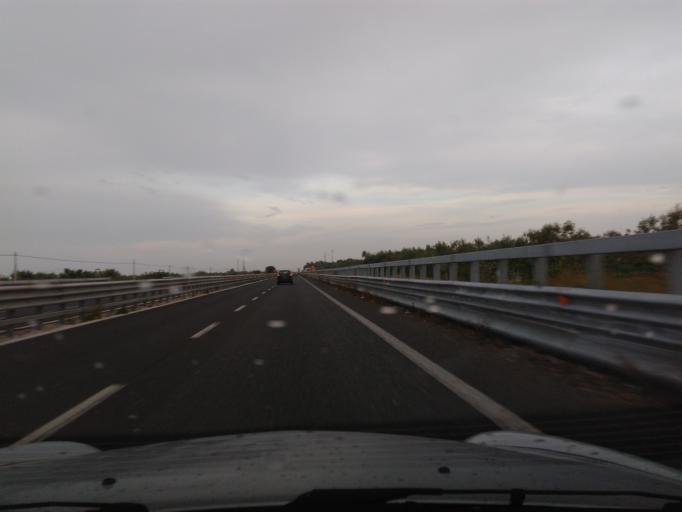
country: IT
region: Apulia
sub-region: Provincia di Bari
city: Giovinazzo
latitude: 41.1698
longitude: 16.6981
